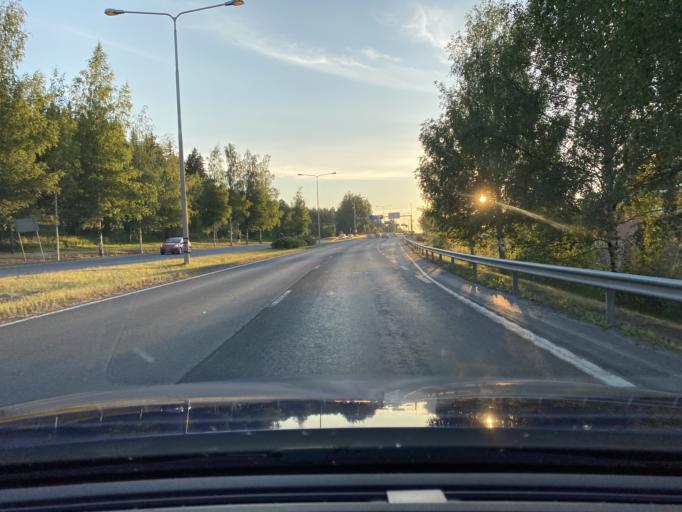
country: FI
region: Pirkanmaa
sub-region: Tampere
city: Pirkkala
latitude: 61.5140
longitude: 23.6661
